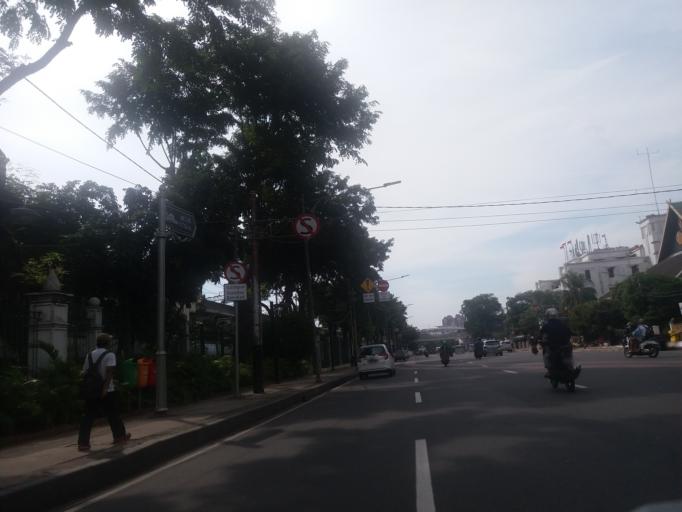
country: ID
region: Jakarta Raya
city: Jakarta
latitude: -6.1765
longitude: 106.8310
